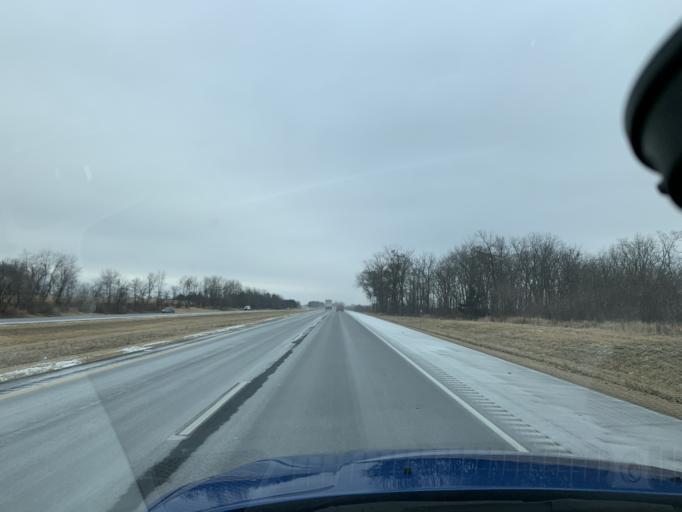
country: US
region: Wisconsin
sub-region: Dane County
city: Sun Prairie
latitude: 43.2474
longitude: -89.1373
